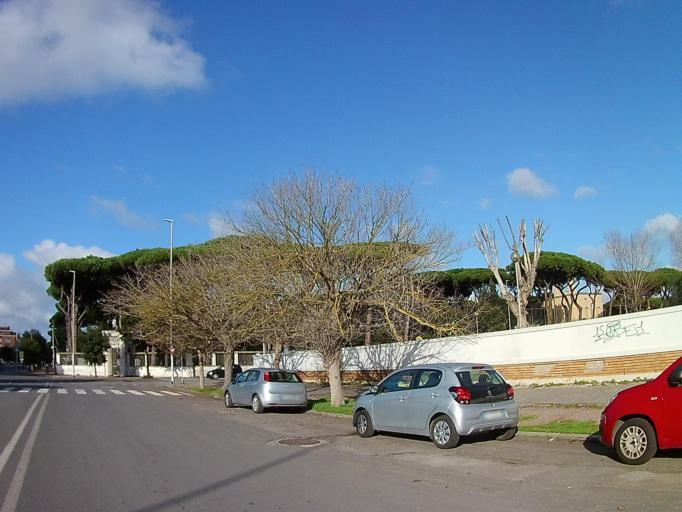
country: IT
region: Latium
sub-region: Citta metropolitana di Roma Capitale
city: Lido di Ostia
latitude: 41.7284
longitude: 12.2962
